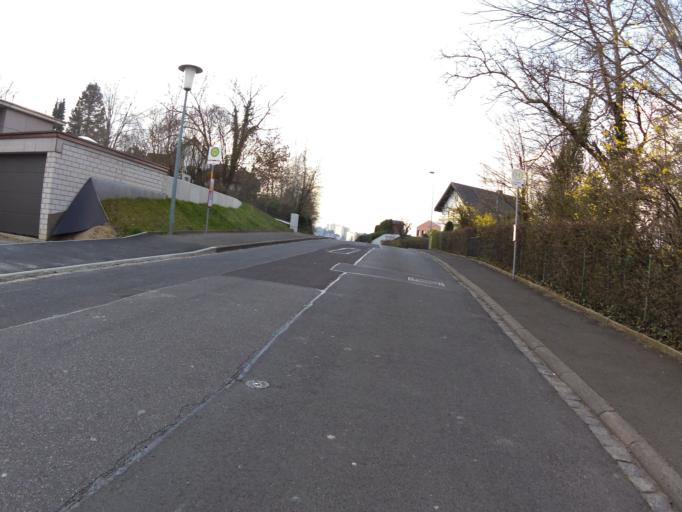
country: DE
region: Bavaria
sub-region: Regierungsbezirk Unterfranken
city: Kitzingen
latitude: 49.7410
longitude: 10.1555
